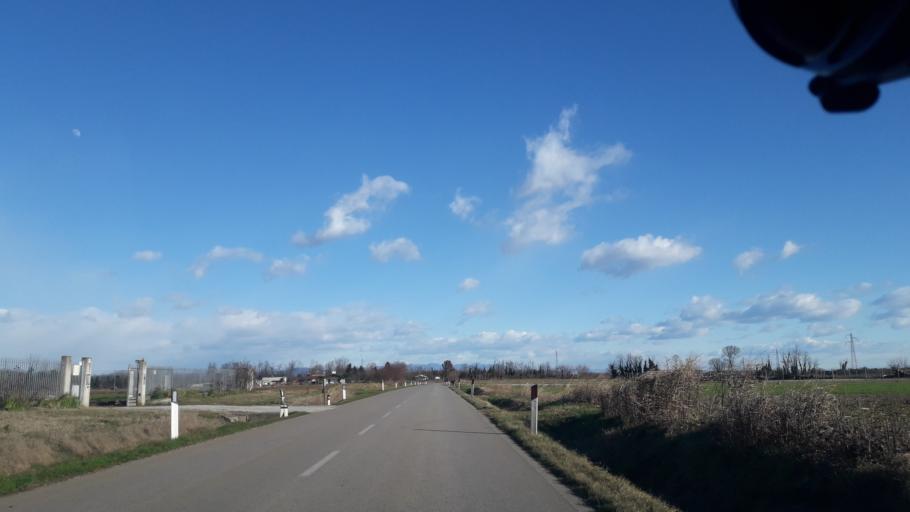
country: IT
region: Friuli Venezia Giulia
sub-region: Provincia di Udine
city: Martignacco
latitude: 46.0755
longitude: 13.1573
